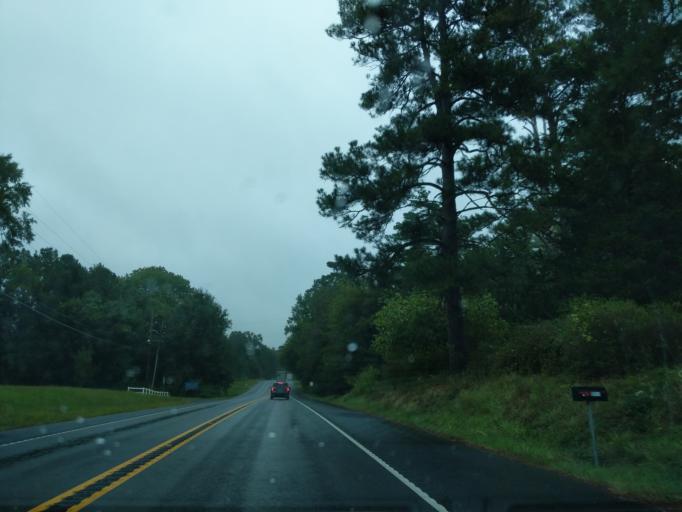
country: US
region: Louisiana
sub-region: Caddo Parish
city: Greenwood
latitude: 32.3789
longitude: -94.0292
